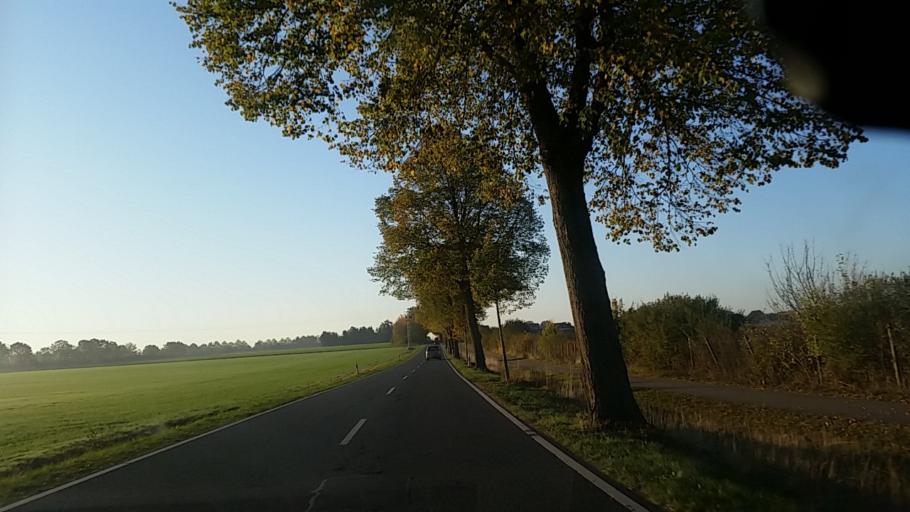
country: DE
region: Lower Saxony
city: Jembke
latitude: 52.4834
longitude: 10.7715
